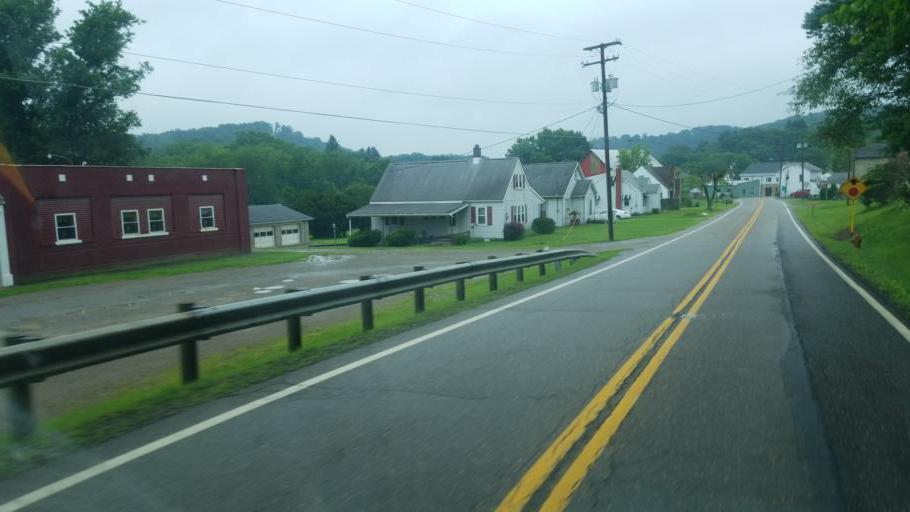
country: US
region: Ohio
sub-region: Columbiana County
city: Salineville
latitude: 40.4711
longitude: -80.9261
